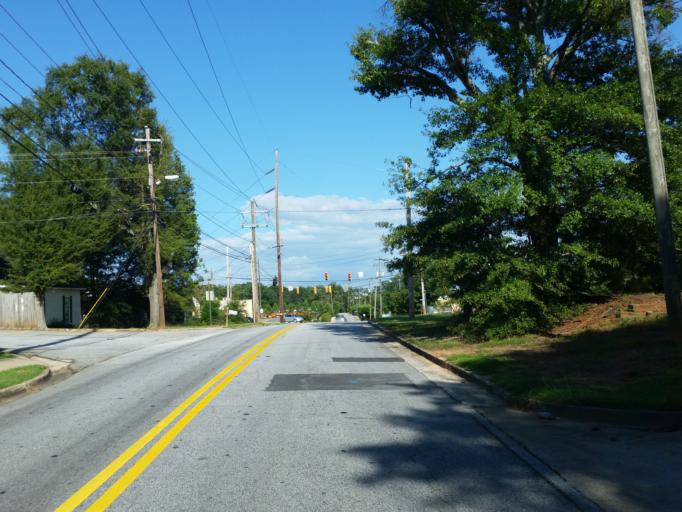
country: US
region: Georgia
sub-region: Cobb County
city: Smyrna
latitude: 33.8906
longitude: -84.5065
